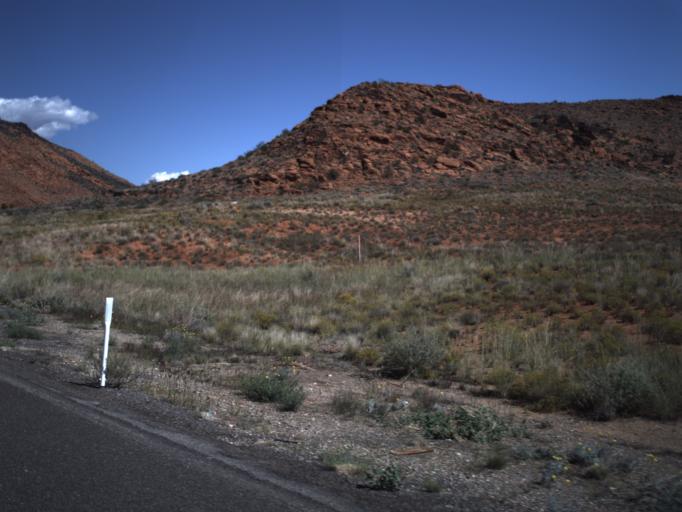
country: US
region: Utah
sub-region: Washington County
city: Santa Clara
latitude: 37.1524
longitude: -113.6067
